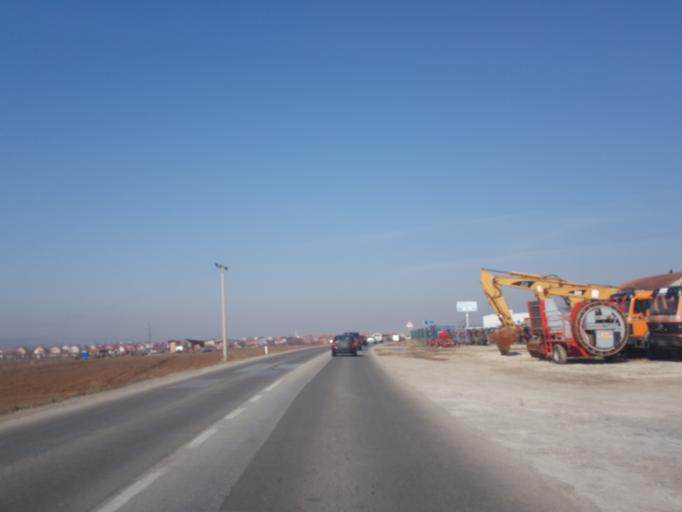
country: XK
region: Mitrovica
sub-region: Vushtrri
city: Vushtrri
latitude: 42.7748
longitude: 21.0165
